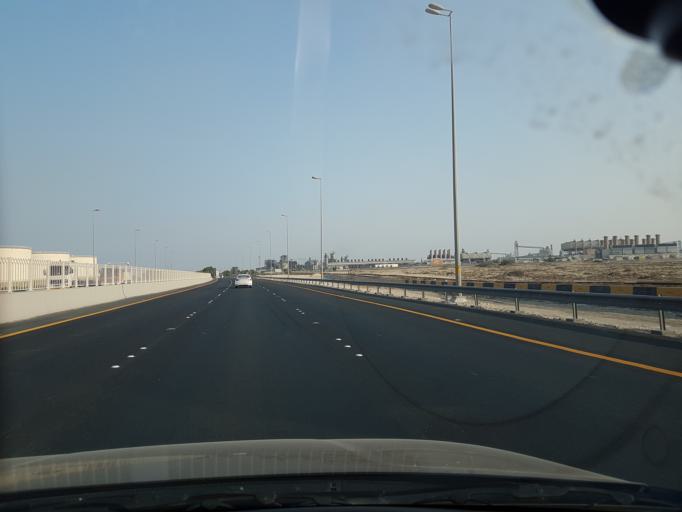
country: BH
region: Northern
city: Ar Rifa'
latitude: 26.1029
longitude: 50.6023
